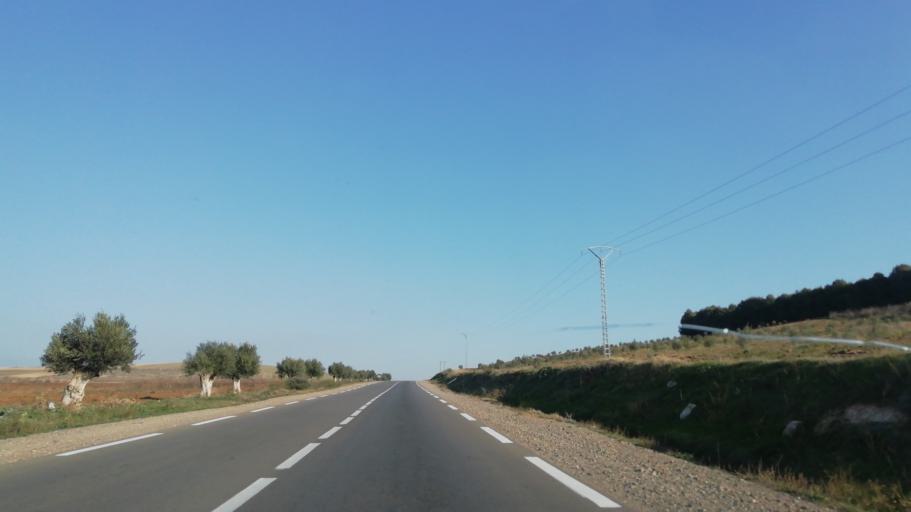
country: DZ
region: Ain Temouchent
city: Hammam Bou Hadjar
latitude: 35.1653
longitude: -0.8812
